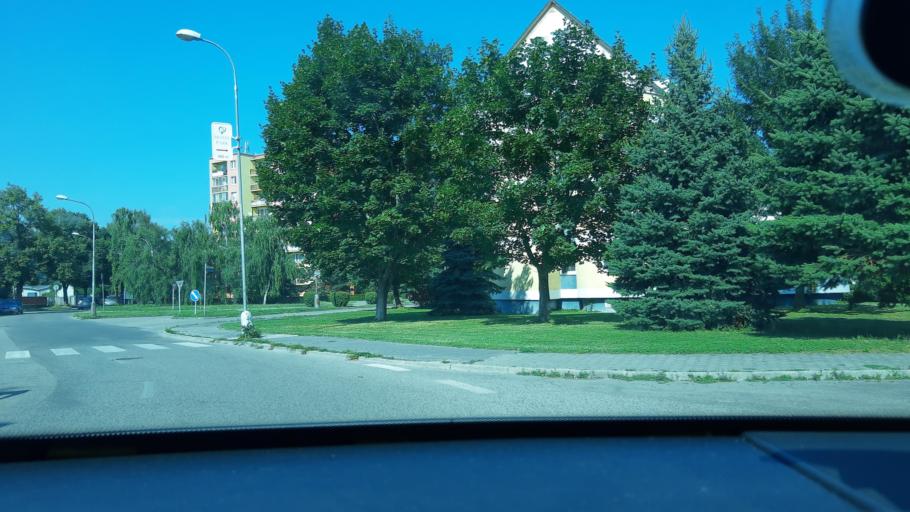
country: SK
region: Trnavsky
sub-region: Okres Trnava
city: Piestany
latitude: 48.5990
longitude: 17.8348
